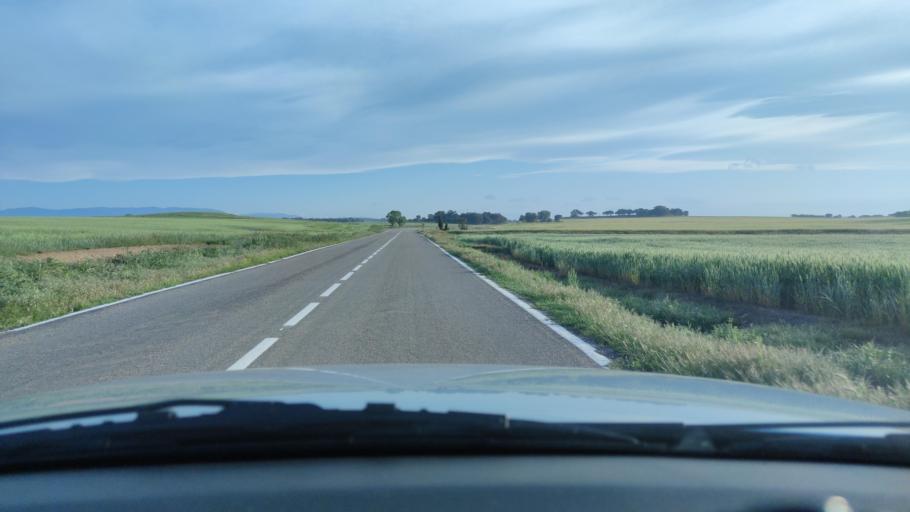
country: ES
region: Catalonia
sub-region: Provincia de Lleida
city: Agramunt
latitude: 41.8099
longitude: 1.0529
